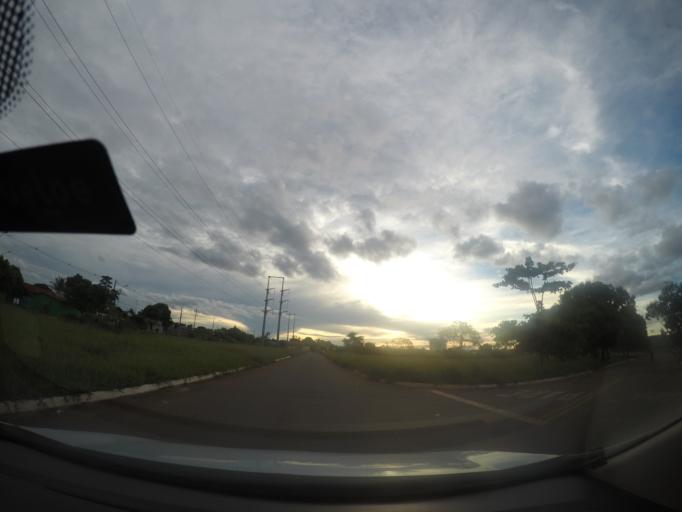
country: BR
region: Goias
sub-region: Goianira
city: Goianira
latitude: -16.5849
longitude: -49.3761
